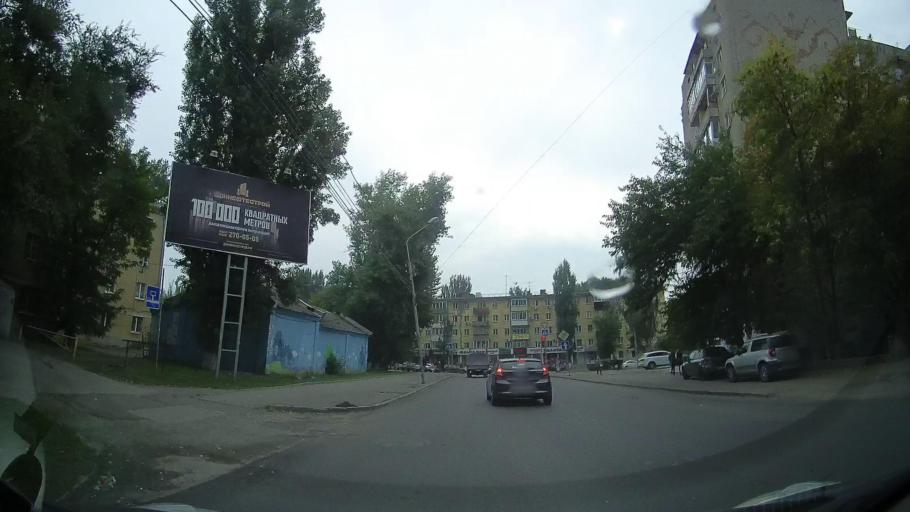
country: RU
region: Rostov
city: Rostov-na-Donu
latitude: 47.2505
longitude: 39.7065
